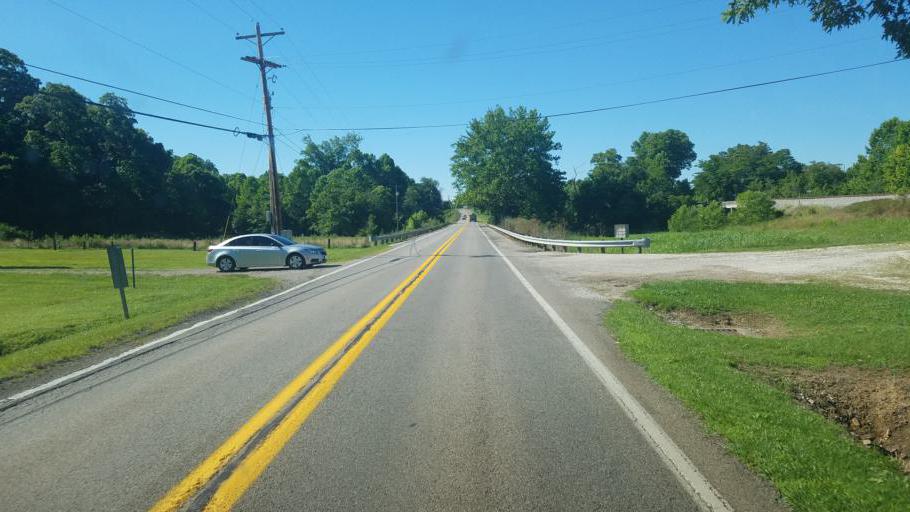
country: US
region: Ohio
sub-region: Gallia County
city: Gallipolis
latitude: 38.6928
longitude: -82.1762
